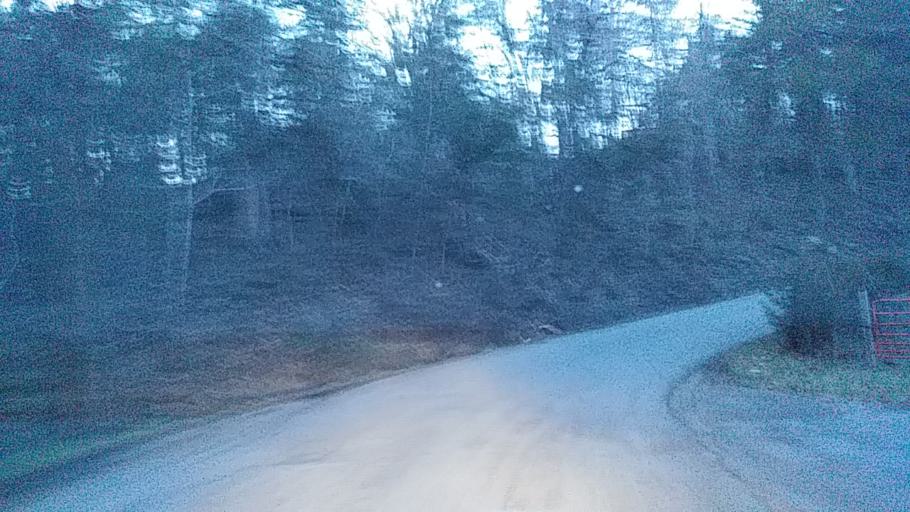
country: US
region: Tennessee
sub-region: Greene County
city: Mosheim
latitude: 36.0632
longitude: -82.9873
